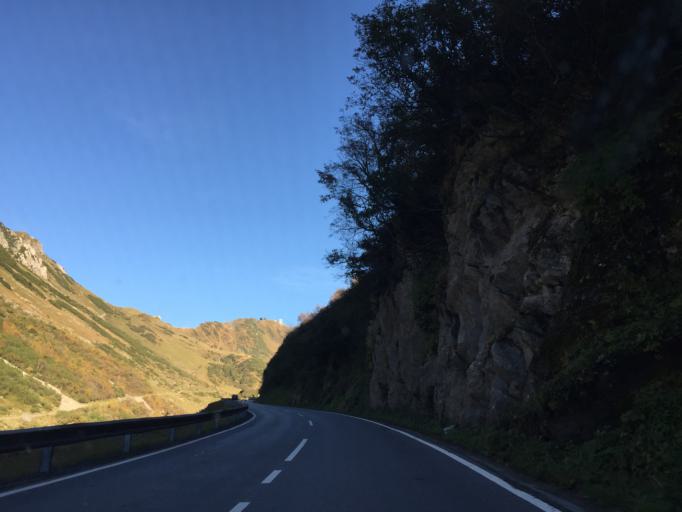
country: AT
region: Tyrol
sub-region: Politischer Bezirk Landeck
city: Sankt Anton am Arlberg
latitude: 47.1370
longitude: 10.1867
